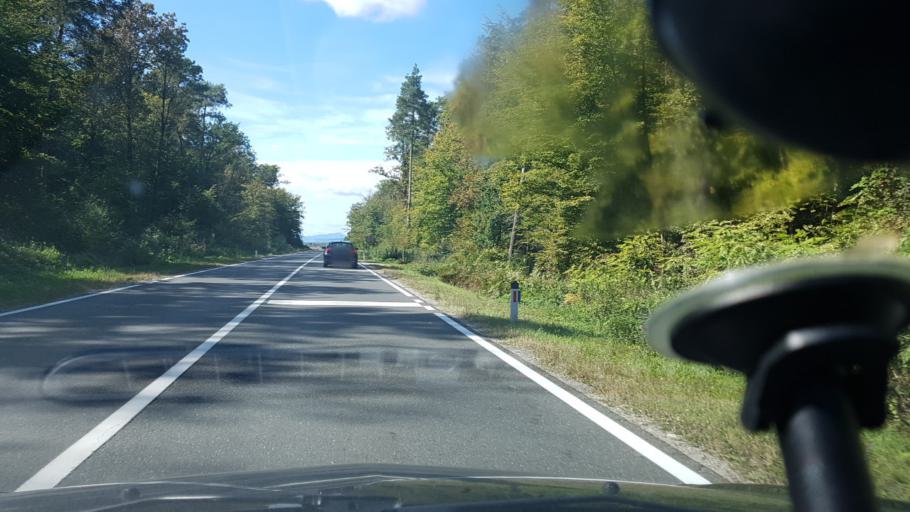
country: SI
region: Kidricevo
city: Kidricevo
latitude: 46.4099
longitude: 15.7585
